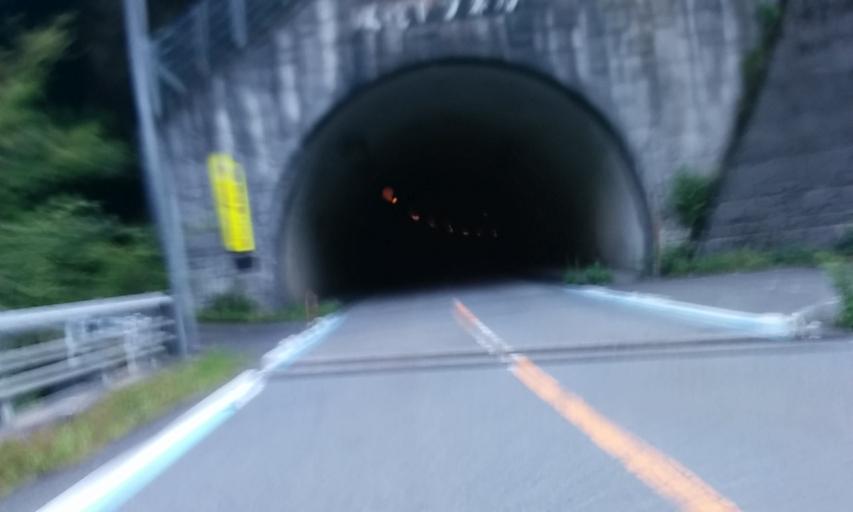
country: JP
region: Ehime
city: Saijo
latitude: 33.8482
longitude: 133.2130
